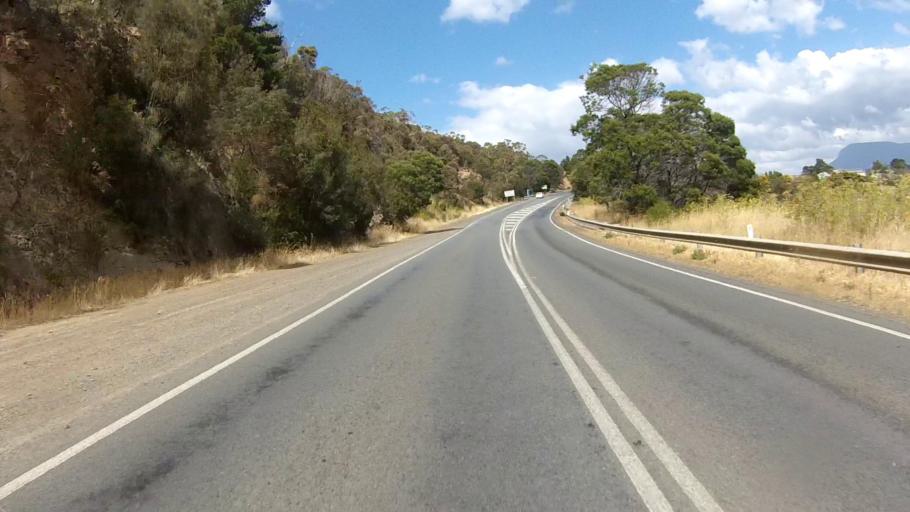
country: AU
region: Tasmania
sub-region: Brighton
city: Old Beach
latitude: -42.7894
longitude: 147.2928
